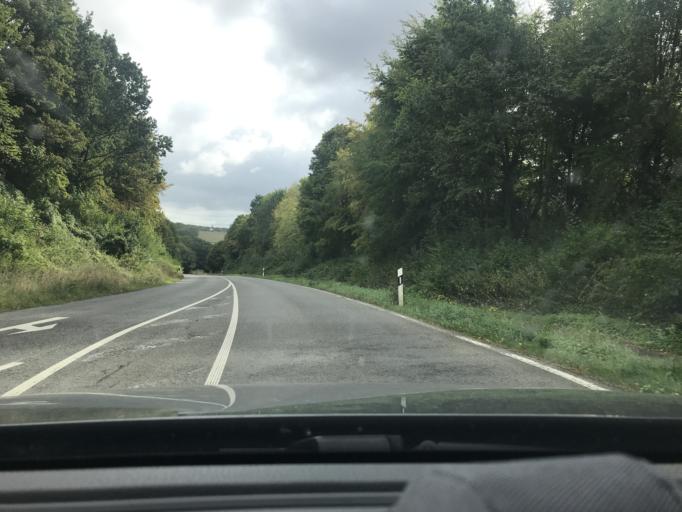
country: DE
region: North Rhine-Westphalia
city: Haan
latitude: 51.2283
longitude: 7.0047
